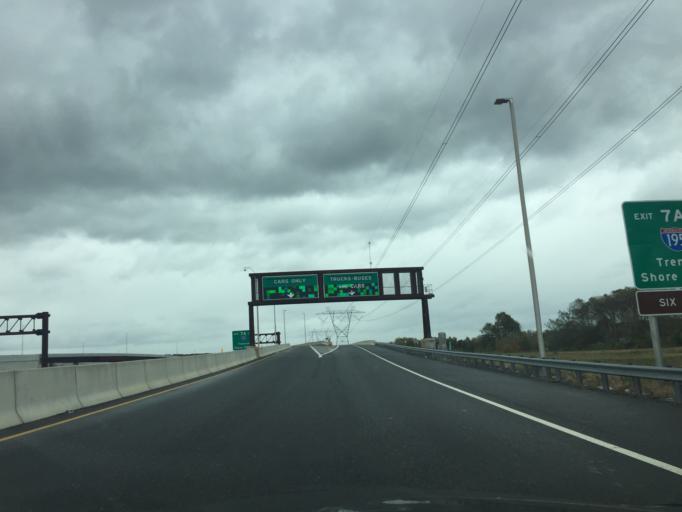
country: US
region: New Jersey
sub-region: Mercer County
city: Robbinsville
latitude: 40.1783
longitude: -74.6270
